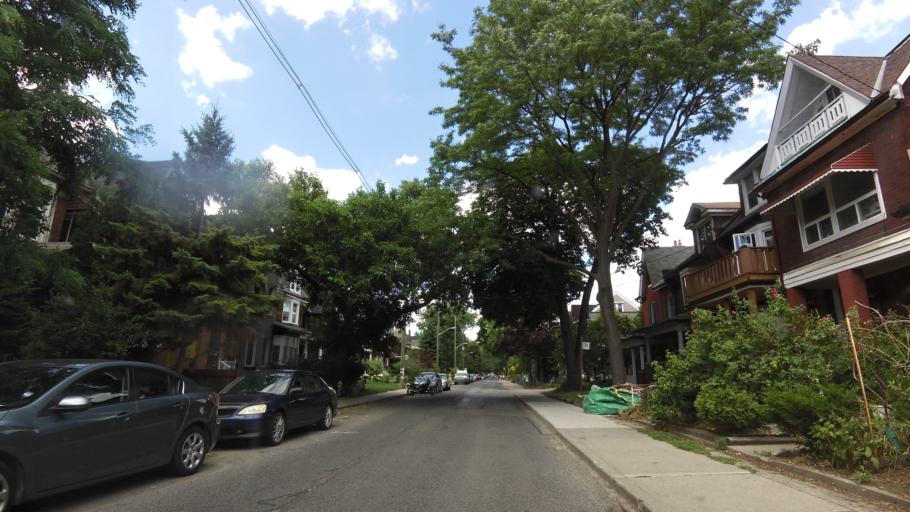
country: CA
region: Ontario
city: Toronto
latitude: 43.6405
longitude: -79.4412
